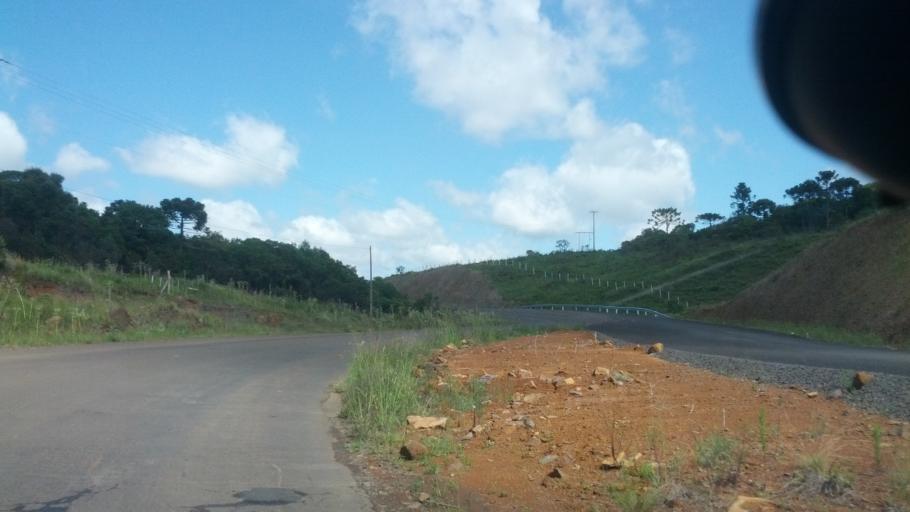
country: BR
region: Santa Catarina
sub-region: Lages
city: Lages
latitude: -27.9504
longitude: -50.4988
